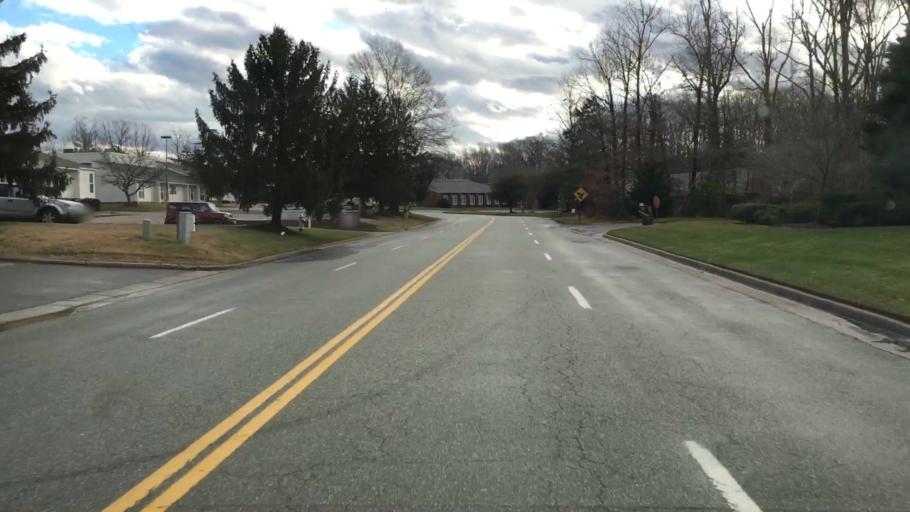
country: US
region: Virginia
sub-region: Chesterfield County
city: Bon Air
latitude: 37.4992
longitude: -77.5994
